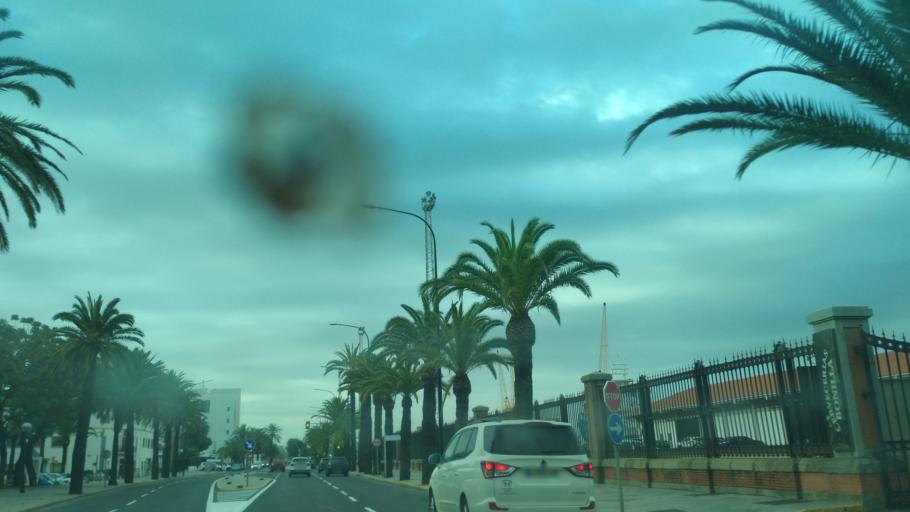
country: ES
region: Andalusia
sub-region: Provincia de Huelva
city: Huelva
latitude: 37.2550
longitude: -6.9591
